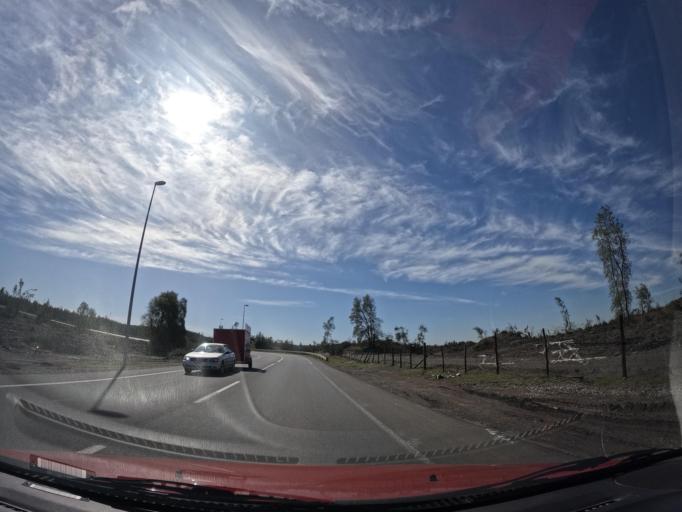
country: CL
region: Biobio
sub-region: Provincia de Biobio
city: Cabrero
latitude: -36.9348
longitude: -72.3446
